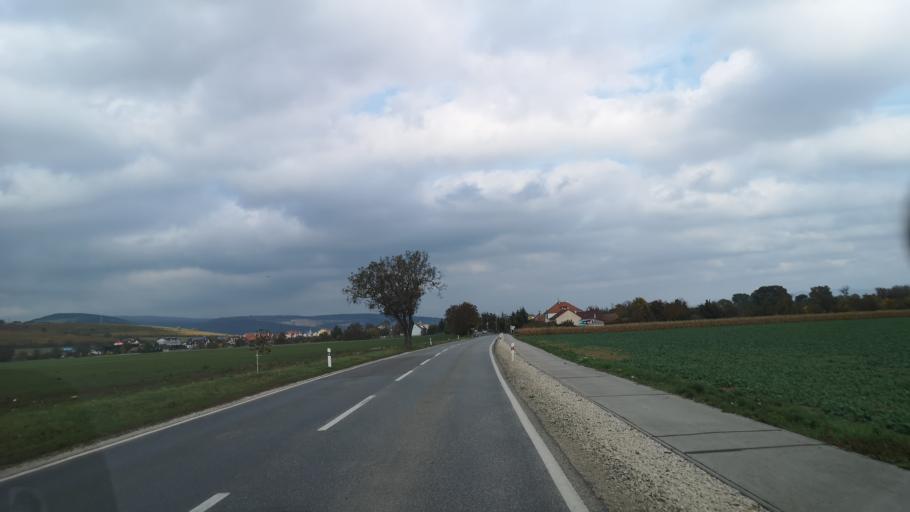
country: SK
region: Nitriansky
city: Cachtice
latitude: 48.6831
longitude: 17.7767
